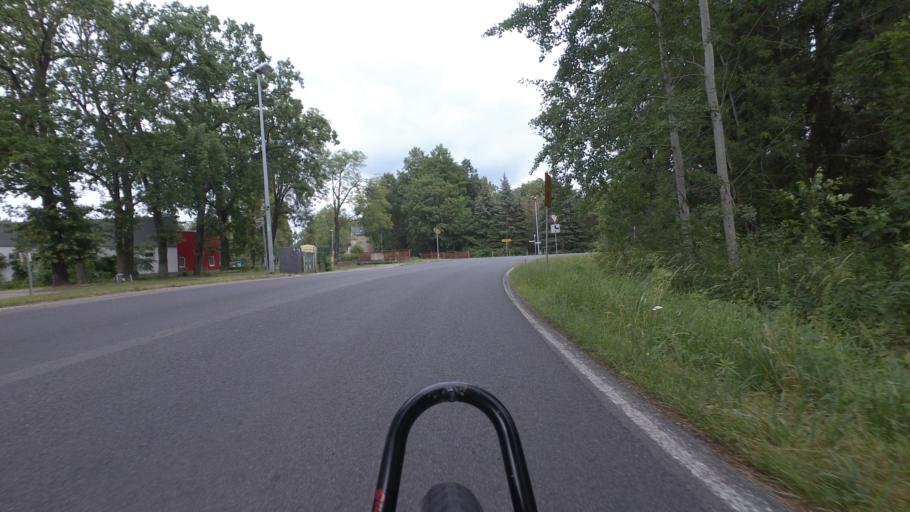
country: DE
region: Brandenburg
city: Am Mellensee
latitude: 52.1809
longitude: 13.3978
